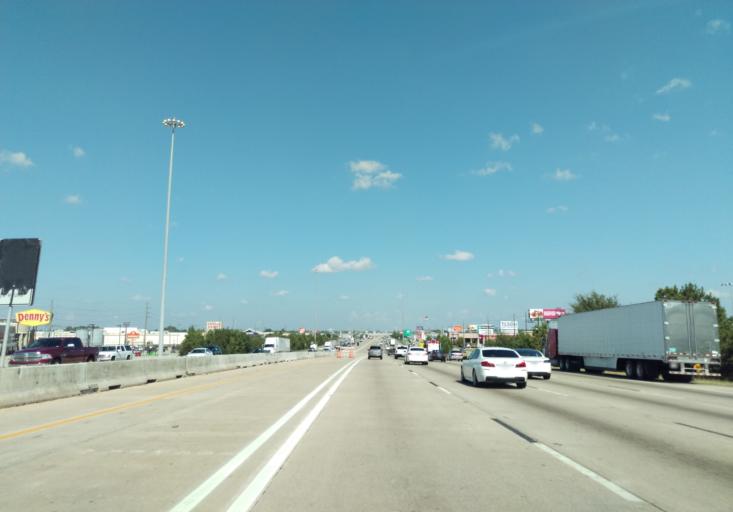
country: US
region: Texas
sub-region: Harris County
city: Spring
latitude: 30.0534
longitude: -95.4320
